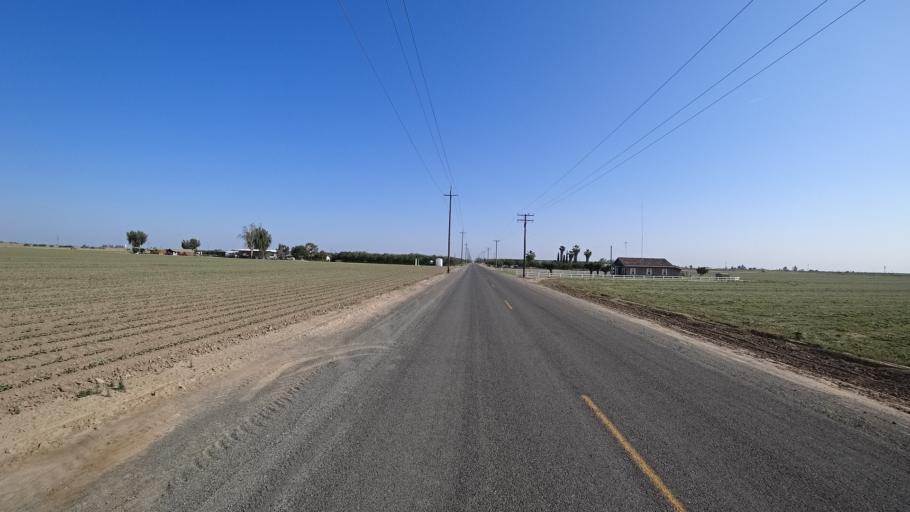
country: US
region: California
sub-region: Kings County
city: Home Garden
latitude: 36.3024
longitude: -119.5831
